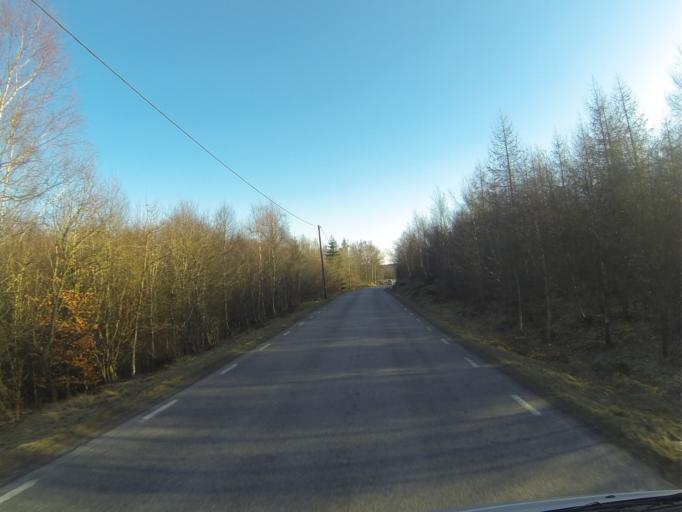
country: SE
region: Skane
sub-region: Horby Kommun
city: Hoerby
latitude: 55.8992
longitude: 13.6615
